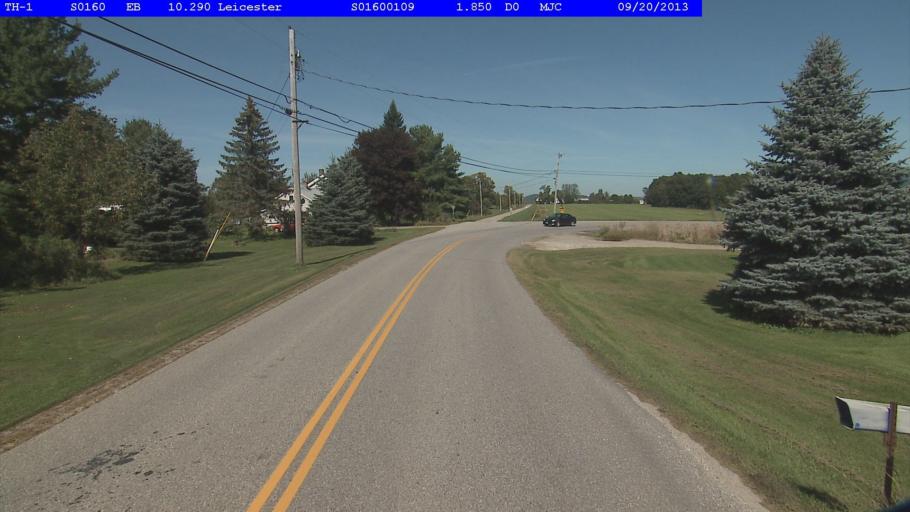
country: US
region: Vermont
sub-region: Rutland County
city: Brandon
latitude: 43.8601
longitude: -73.1296
